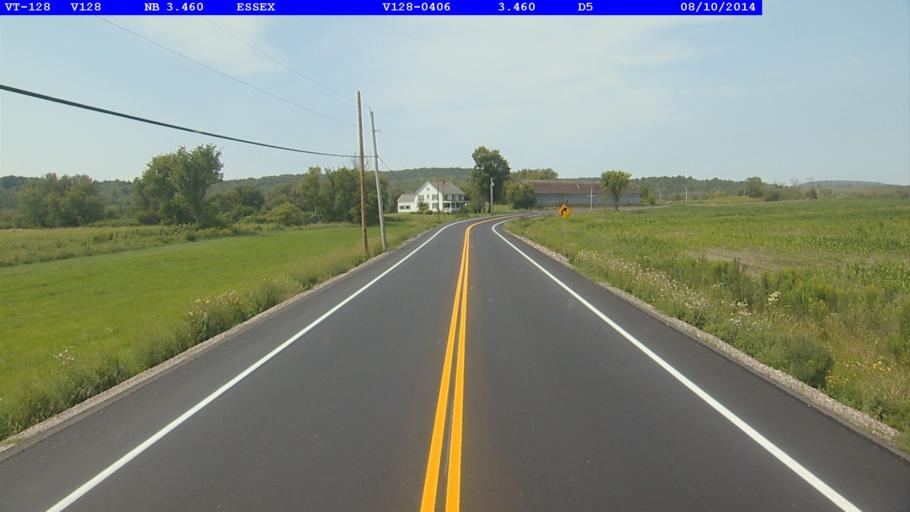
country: US
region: Vermont
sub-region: Chittenden County
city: Jericho
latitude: 44.5473
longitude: -73.0345
